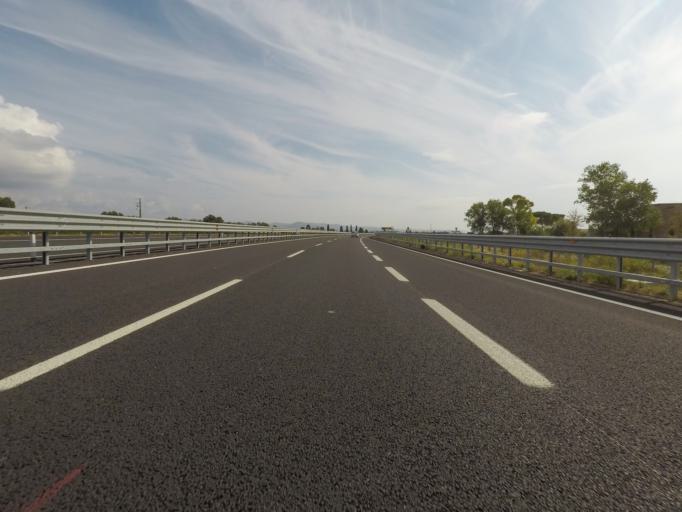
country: IT
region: Latium
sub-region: Provincia di Viterbo
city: Tarquinia
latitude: 42.2328
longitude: 11.7648
